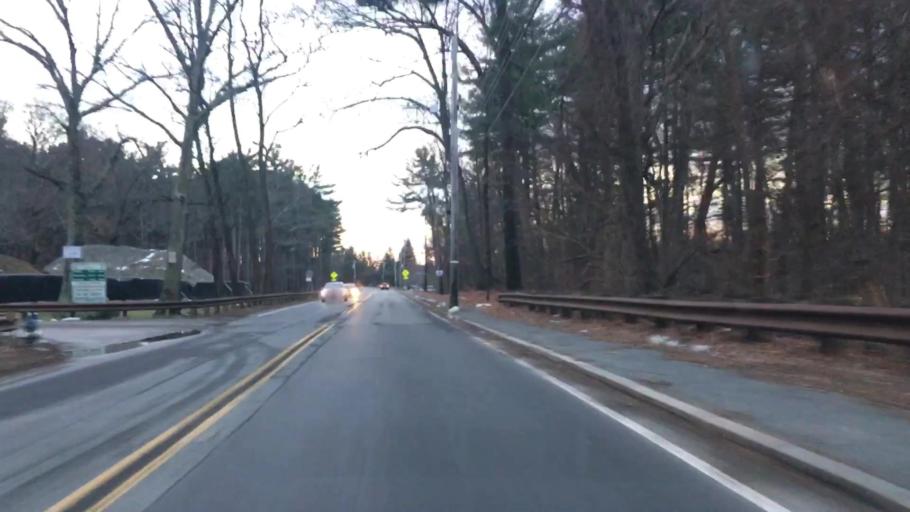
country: US
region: Massachusetts
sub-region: Middlesex County
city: Framingham Center
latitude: 42.2860
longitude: -71.4344
